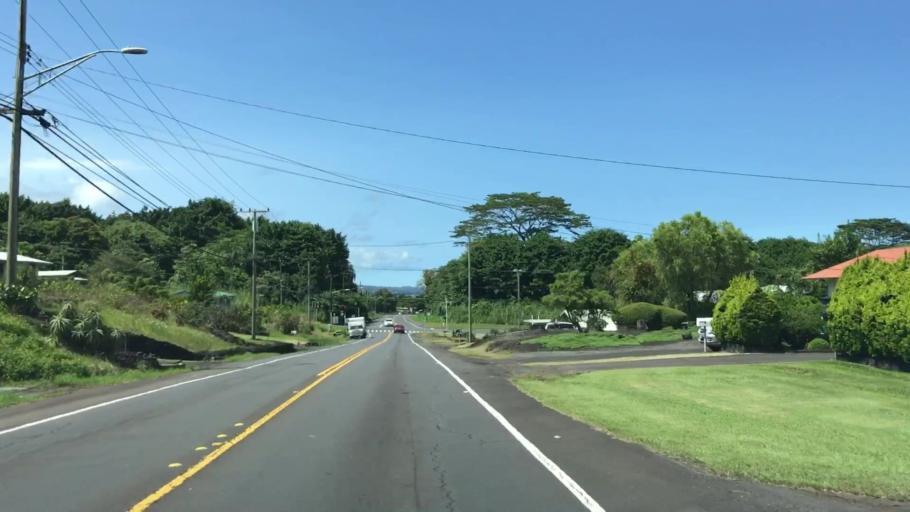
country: US
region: Hawaii
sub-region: Hawaii County
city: Hilo
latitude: 19.6924
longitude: -155.0812
